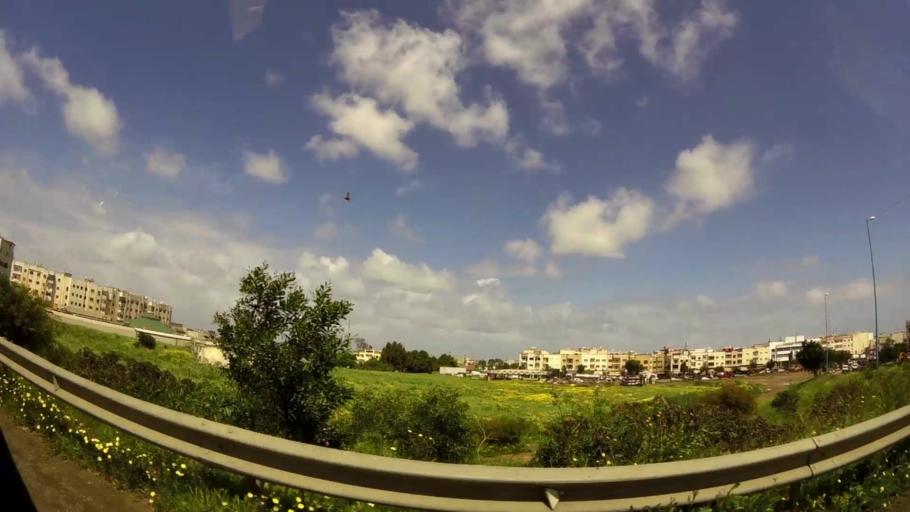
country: MA
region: Grand Casablanca
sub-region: Mediouna
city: Tit Mellil
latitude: 33.6339
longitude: -7.4529
